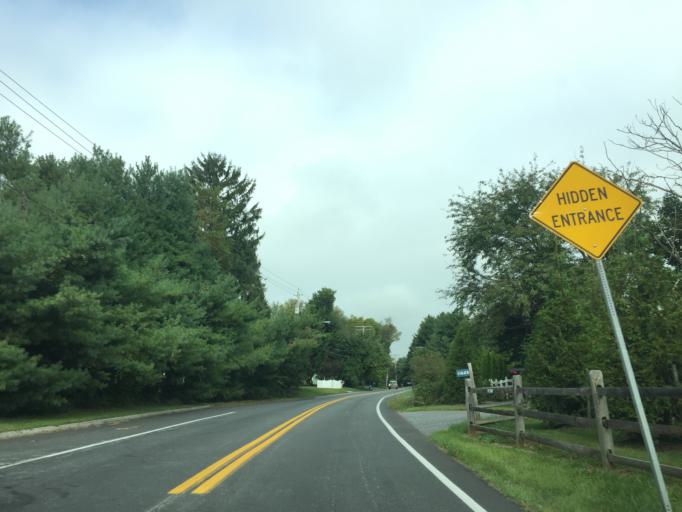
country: US
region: Maryland
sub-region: Baltimore County
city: Garrison
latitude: 39.4432
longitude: -76.7164
